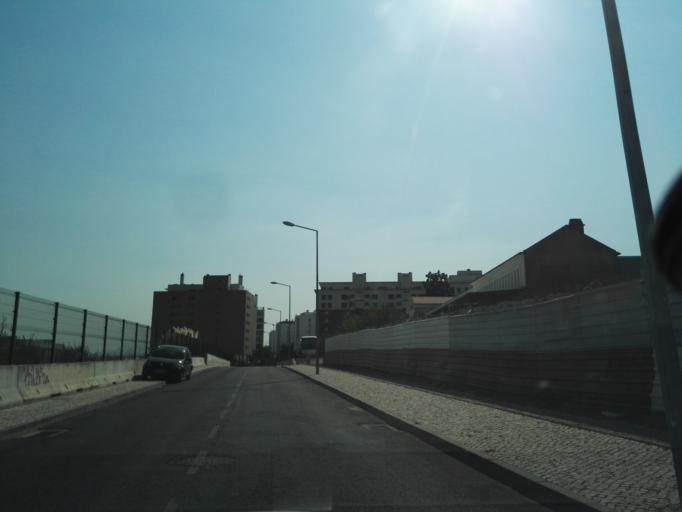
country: PT
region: Lisbon
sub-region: Loures
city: Moscavide
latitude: 38.7511
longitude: -9.1023
